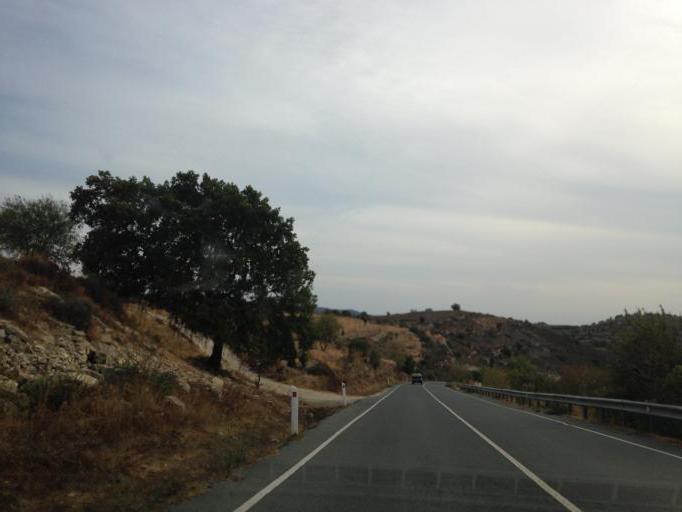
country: CY
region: Limassol
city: Pachna
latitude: 34.8152
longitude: 32.7935
